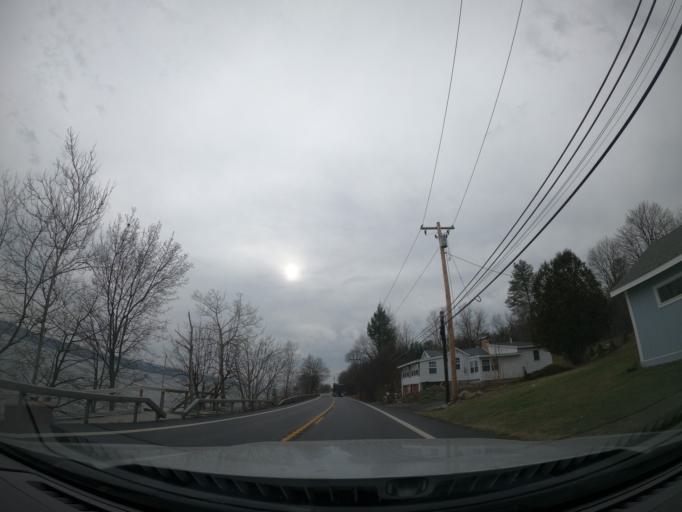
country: US
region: New York
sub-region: Cayuga County
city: Melrose Park
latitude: 42.8556
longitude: -76.5316
